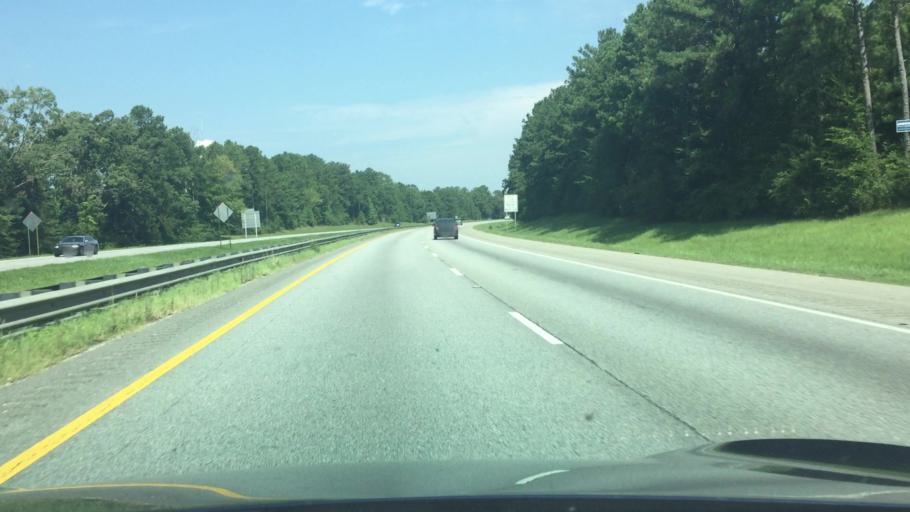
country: US
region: Alabama
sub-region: Shelby County
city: Calera
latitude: 33.1526
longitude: -86.7649
